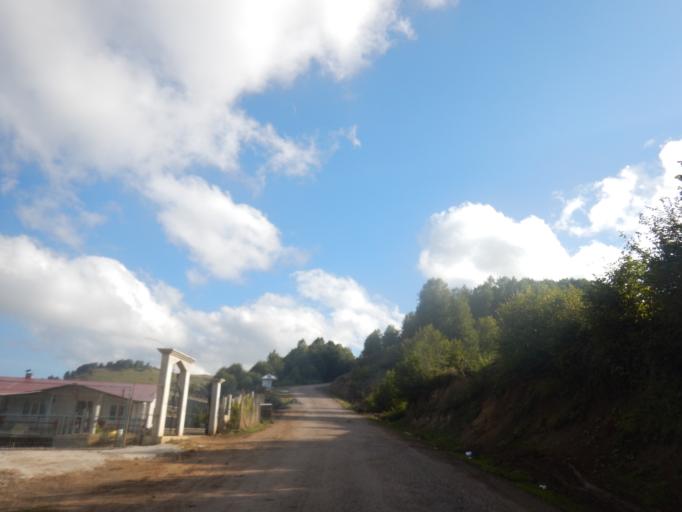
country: TR
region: Ordu
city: Golkoy
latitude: 40.6481
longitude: 37.5498
